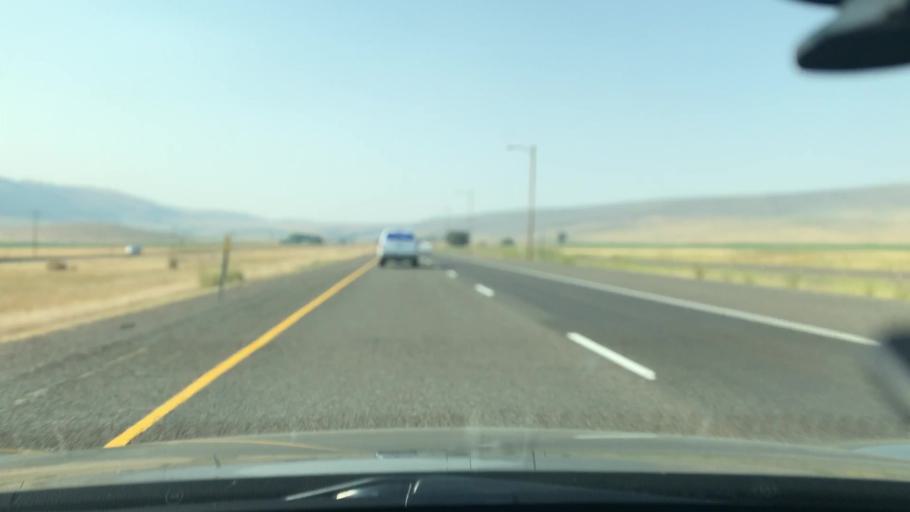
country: US
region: Oregon
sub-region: Union County
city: Union
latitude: 45.1076
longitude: -117.9567
